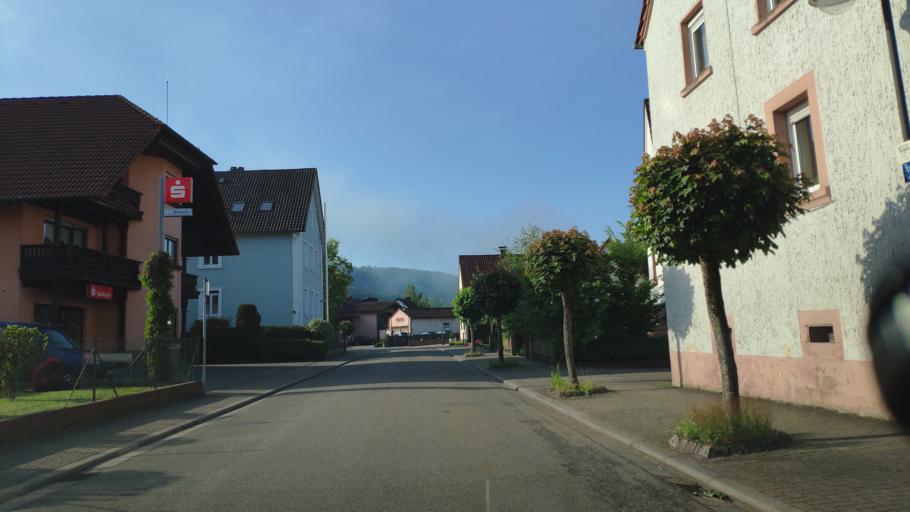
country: DE
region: Rheinland-Pfalz
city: Fischbach
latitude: 49.0865
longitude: 7.7114
